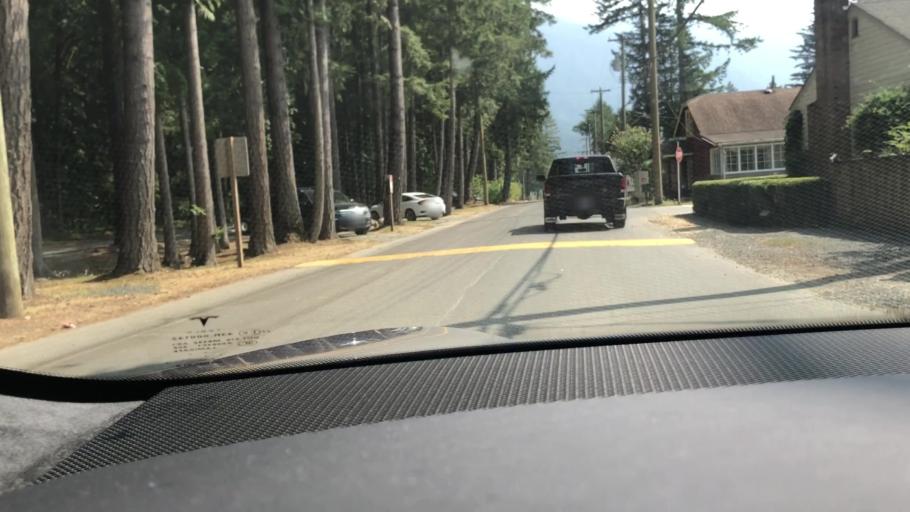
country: CA
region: British Columbia
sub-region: Fraser Valley Regional District
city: Chilliwack
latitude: 49.0700
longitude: -121.9763
